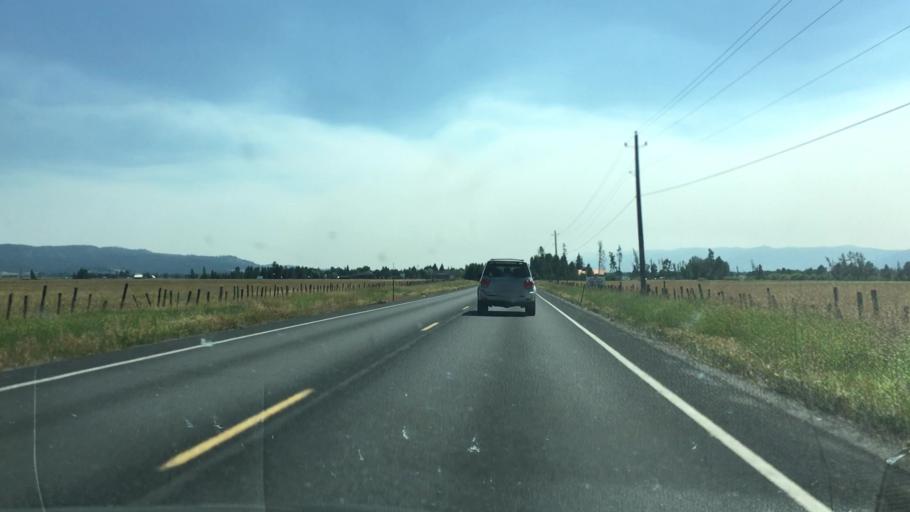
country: US
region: Idaho
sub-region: Valley County
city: McCall
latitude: 44.7451
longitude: -116.0783
